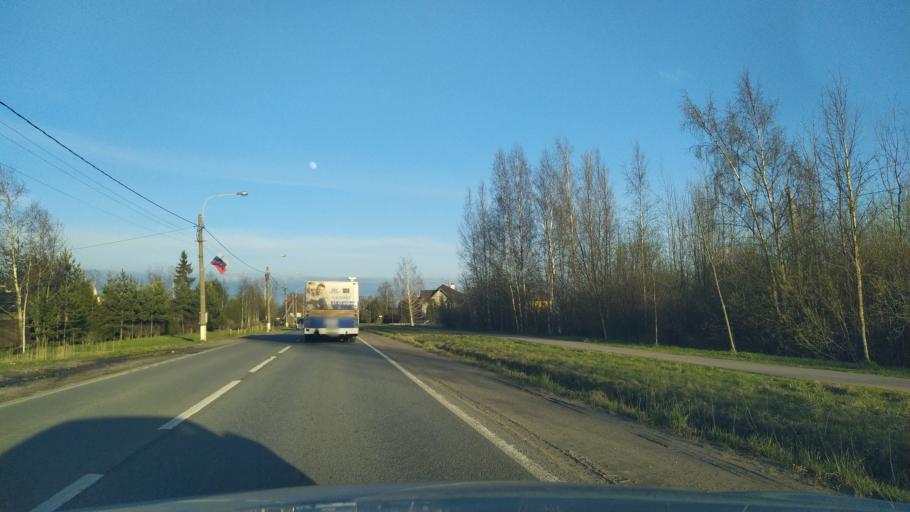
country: RU
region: St.-Petersburg
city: Aleksandrovskaya
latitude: 59.7371
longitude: 30.3305
